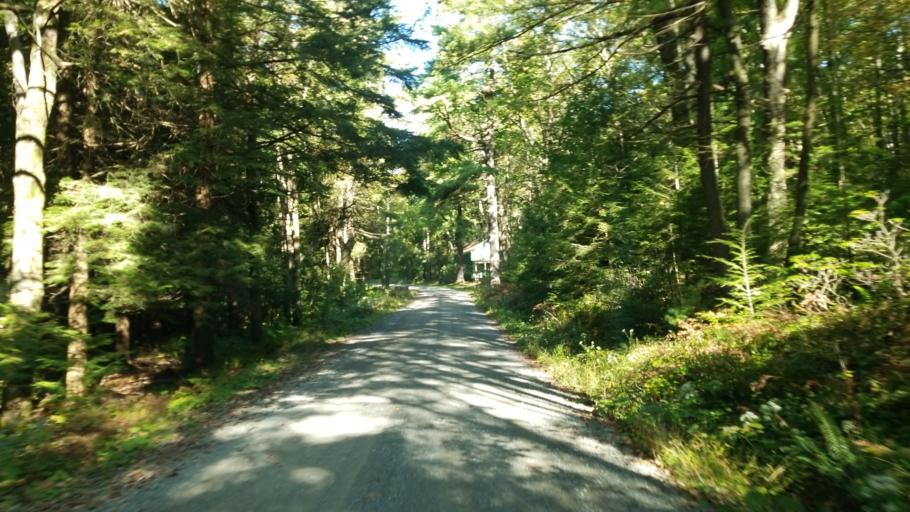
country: US
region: Pennsylvania
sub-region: Clearfield County
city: Hyde
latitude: 41.0878
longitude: -78.5341
